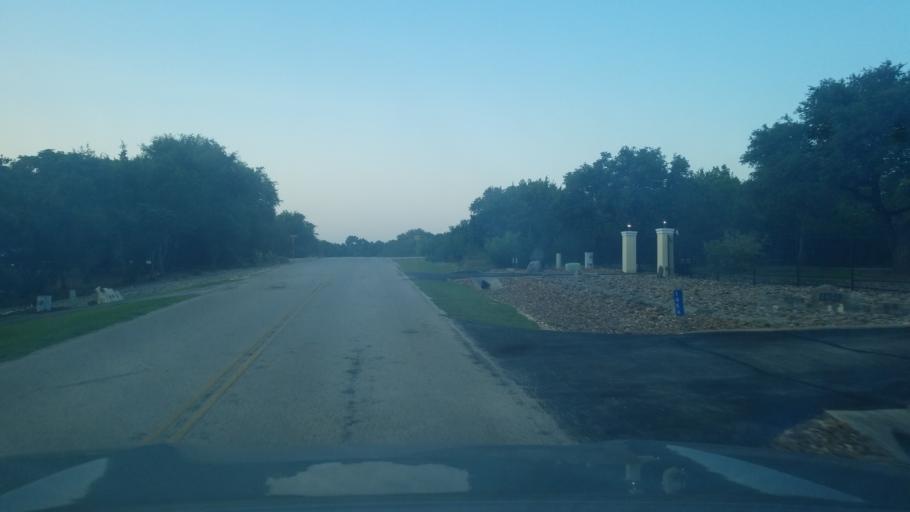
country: US
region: Texas
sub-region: Comal County
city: Bulverde
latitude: 29.8293
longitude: -98.4032
